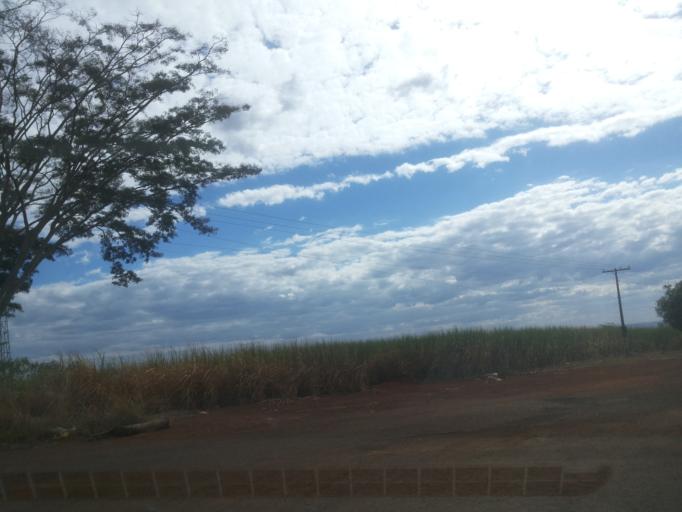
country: BR
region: Minas Gerais
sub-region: Centralina
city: Centralina
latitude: -18.6070
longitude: -49.1937
